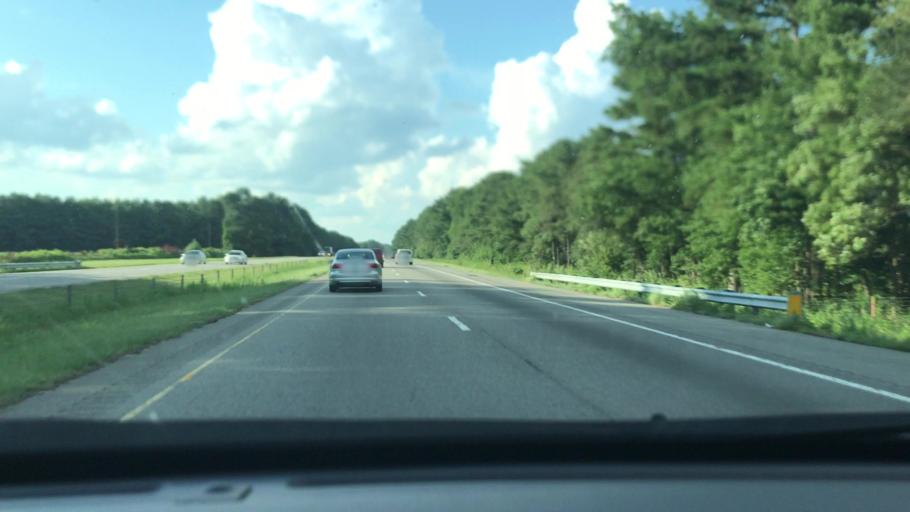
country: US
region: North Carolina
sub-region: Robeson County
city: Saint Pauls
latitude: 34.7534
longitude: -78.9970
